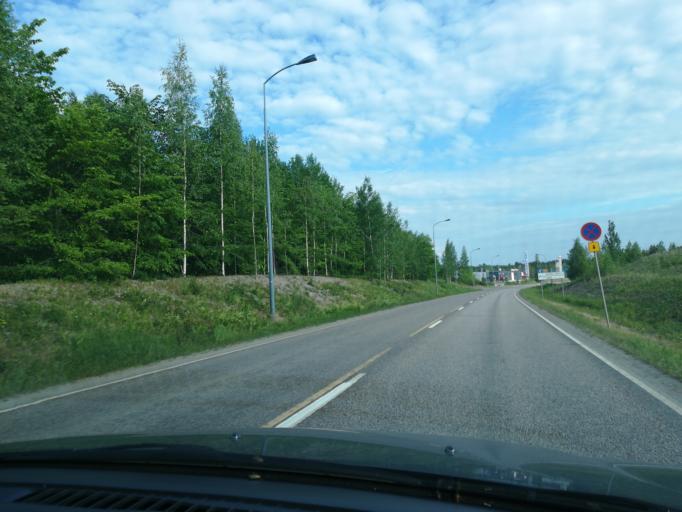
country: FI
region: South Karelia
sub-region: Imatra
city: Imatra
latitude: 61.1531
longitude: 28.8059
